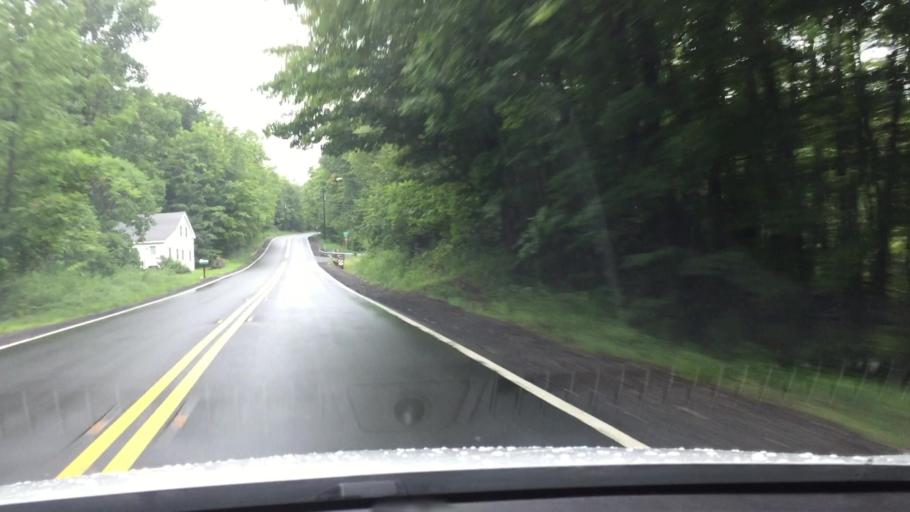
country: US
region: Massachusetts
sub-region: Berkshire County
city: Becket
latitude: 42.3591
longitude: -73.1352
